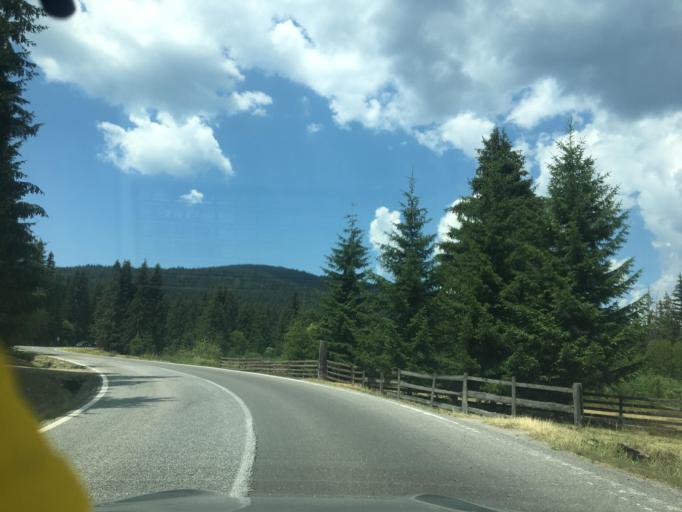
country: RO
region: Harghita
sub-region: Comuna Joseni
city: Joseni
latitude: 46.6755
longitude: 25.3686
